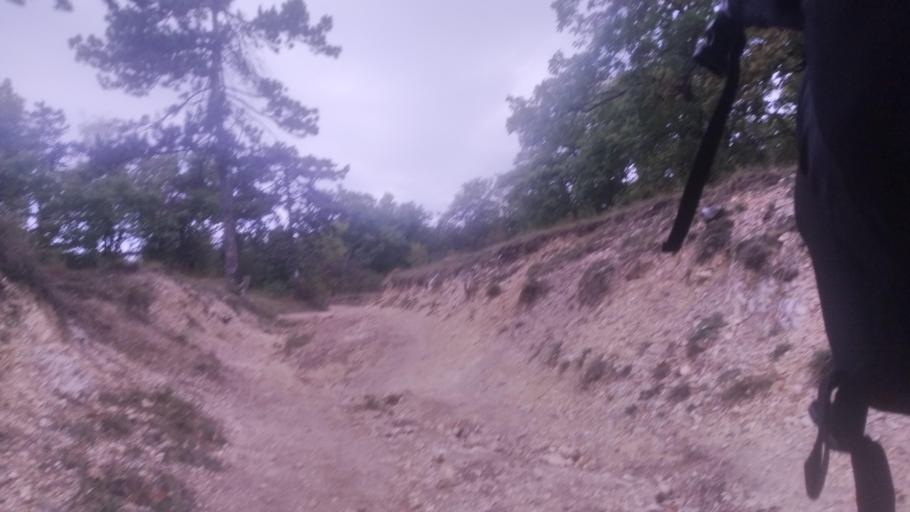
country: HU
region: Pest
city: Telki
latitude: 47.5447
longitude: 18.8700
